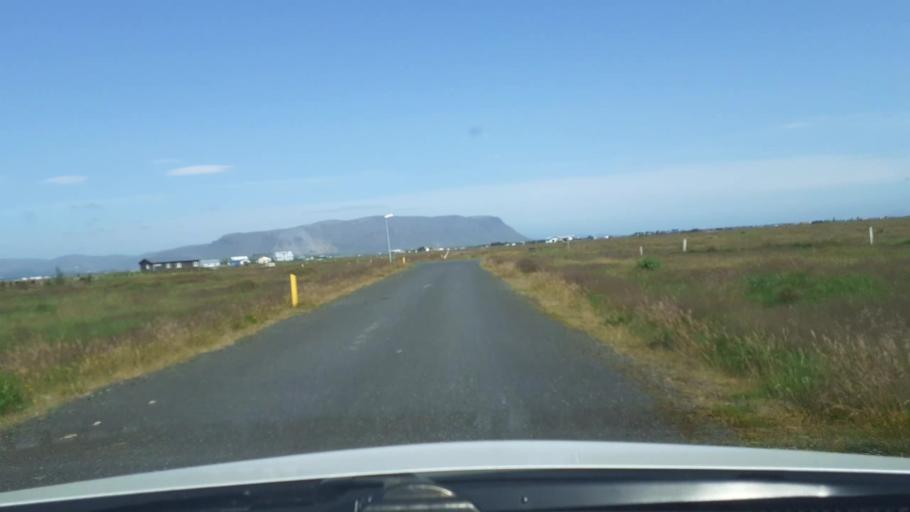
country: IS
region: South
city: Selfoss
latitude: 63.8899
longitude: -21.0857
